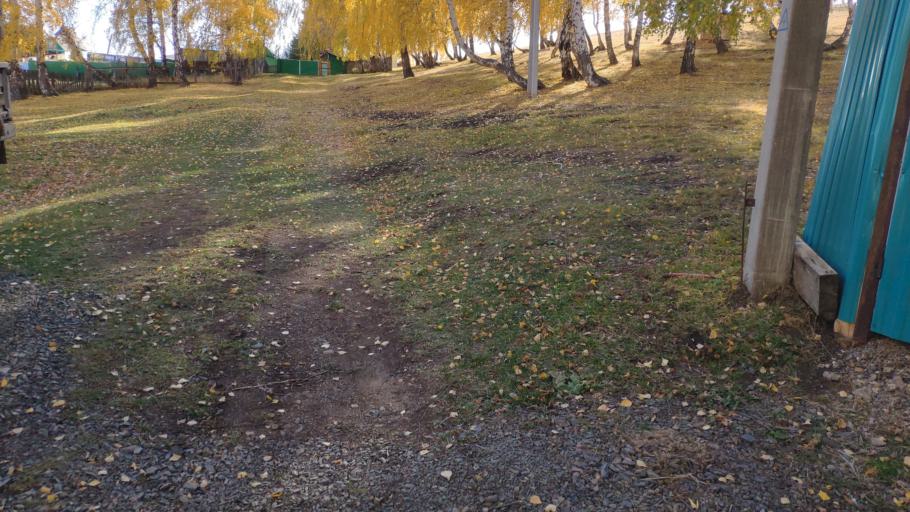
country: RU
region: Bashkortostan
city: Abzakovo
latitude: 53.3436
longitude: 58.5030
